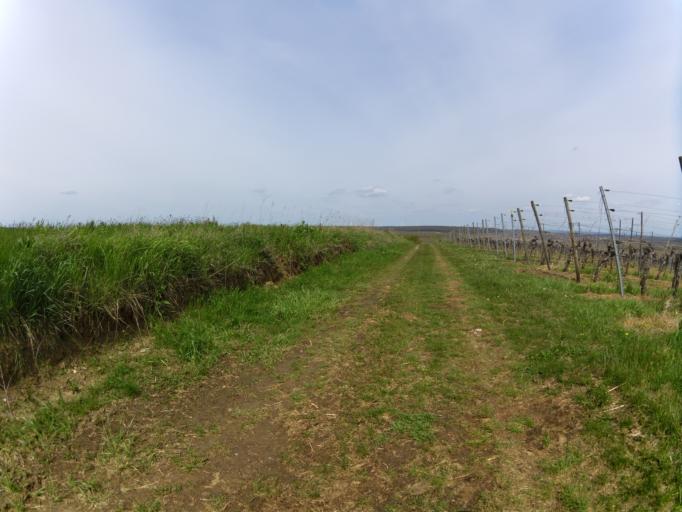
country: DE
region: Bavaria
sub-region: Regierungsbezirk Unterfranken
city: Nordheim
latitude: 49.8591
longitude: 10.1639
